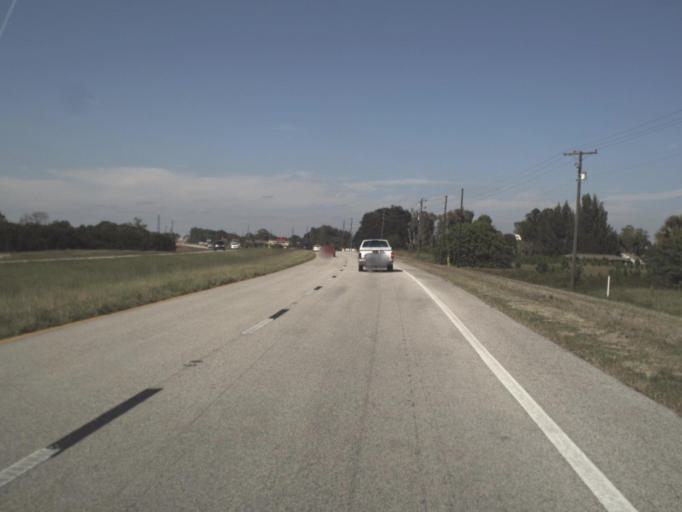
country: US
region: Florida
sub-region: Highlands County
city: Lake Placid
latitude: 27.2315
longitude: -81.3290
